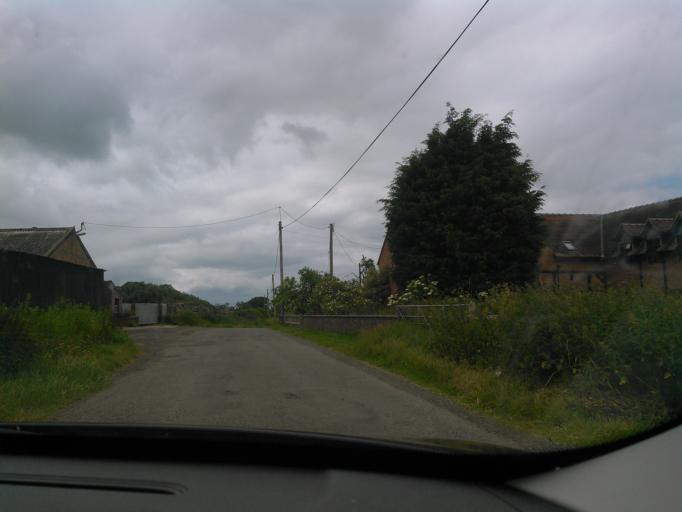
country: GB
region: England
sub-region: Shropshire
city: Wem
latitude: 52.9103
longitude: -2.7472
